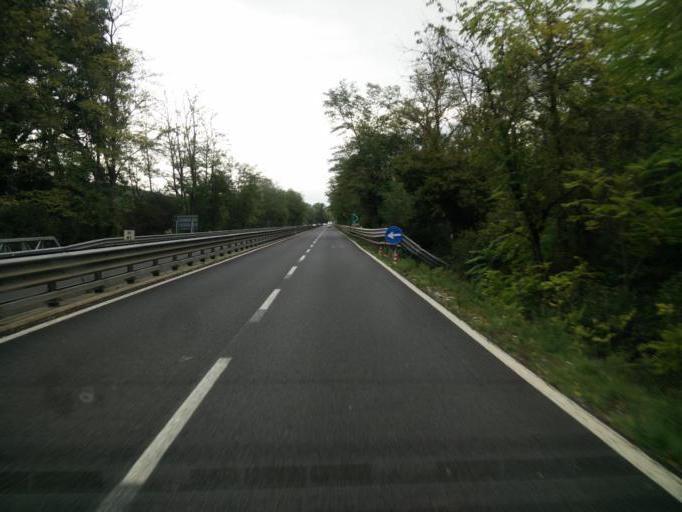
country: IT
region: Tuscany
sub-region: Province of Florence
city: Sambuca
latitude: 43.6001
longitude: 11.1934
